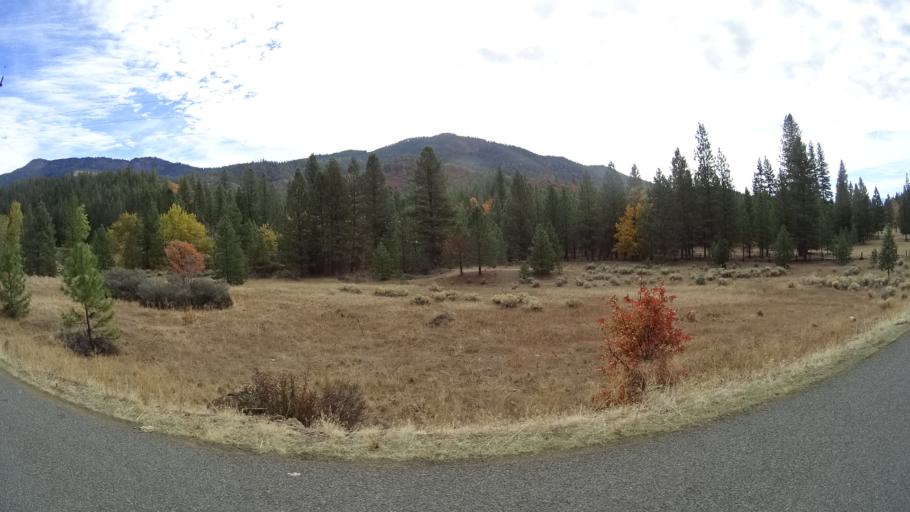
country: US
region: California
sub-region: Siskiyou County
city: Yreka
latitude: 41.6800
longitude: -122.8298
